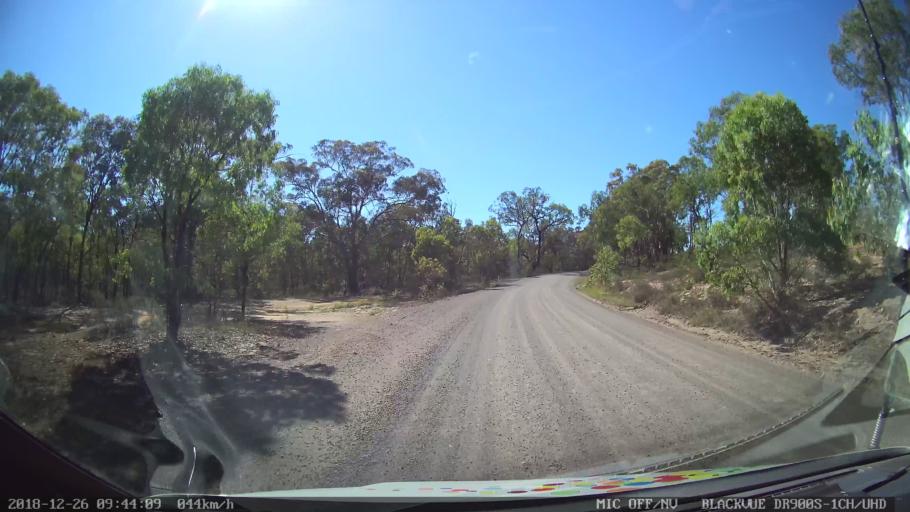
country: AU
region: New South Wales
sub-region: Mid-Western Regional
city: Kandos
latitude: -32.9554
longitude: 150.0954
